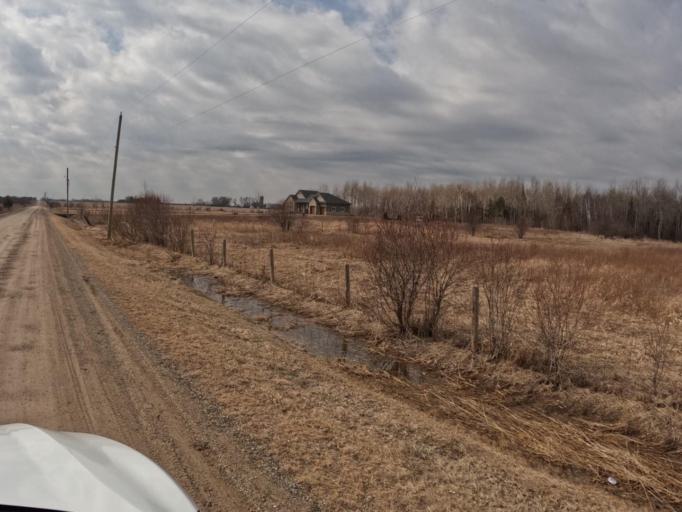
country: CA
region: Ontario
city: Orangeville
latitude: 43.9286
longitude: -80.2198
